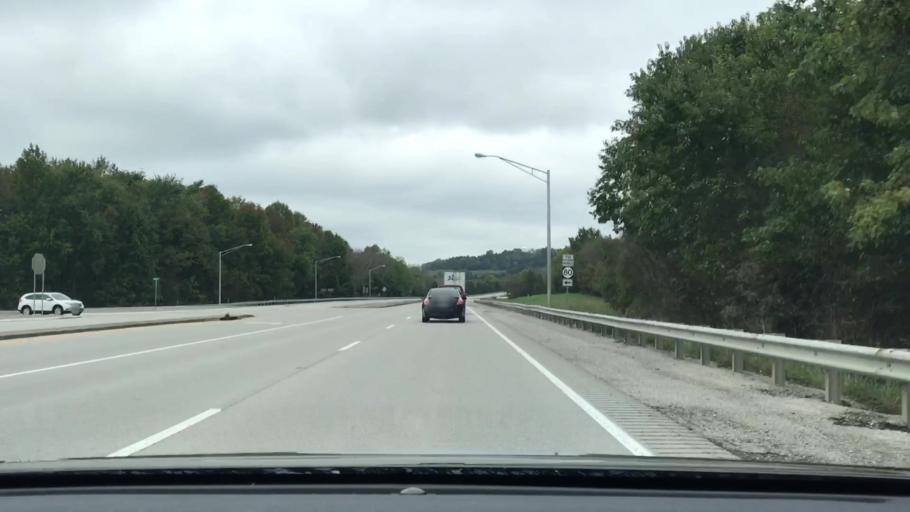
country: US
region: Kentucky
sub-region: Pulaski County
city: Somerset
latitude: 37.0935
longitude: -84.6379
